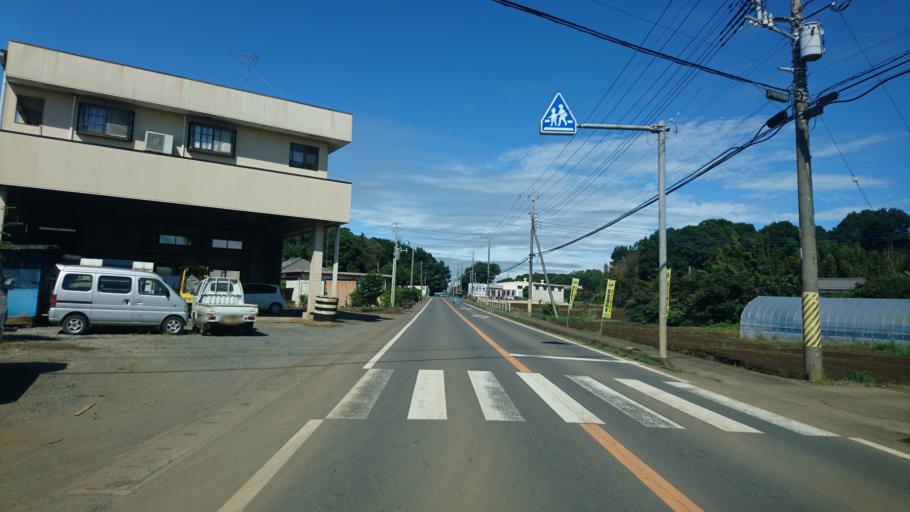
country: JP
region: Ibaraki
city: Ishige
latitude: 36.1448
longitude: 139.9042
